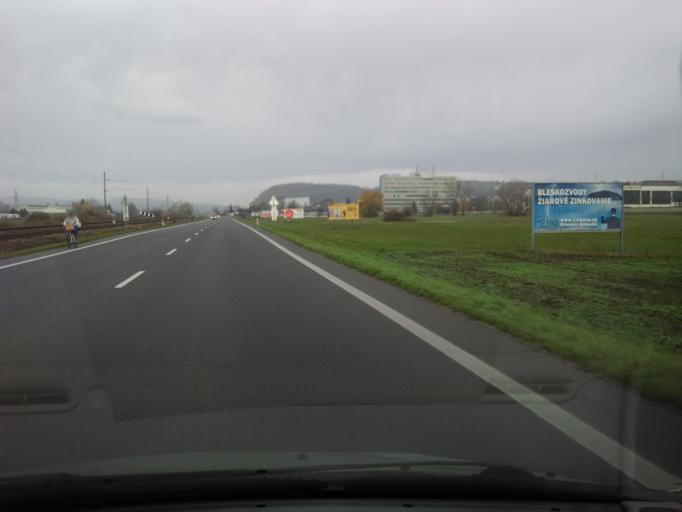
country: SK
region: Nitriansky
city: Tlmace
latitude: 48.2859
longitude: 18.5442
